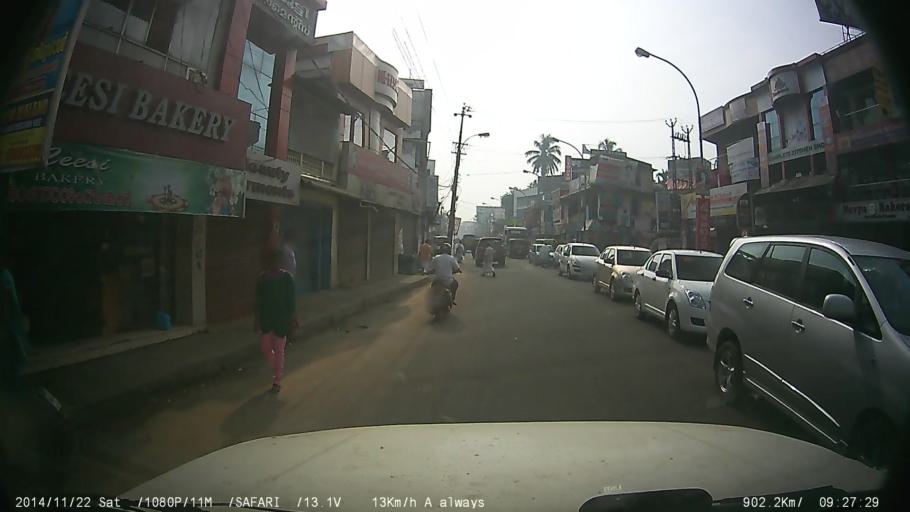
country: IN
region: Kerala
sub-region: Ernakulam
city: Angamali
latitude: 10.1925
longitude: 76.3872
